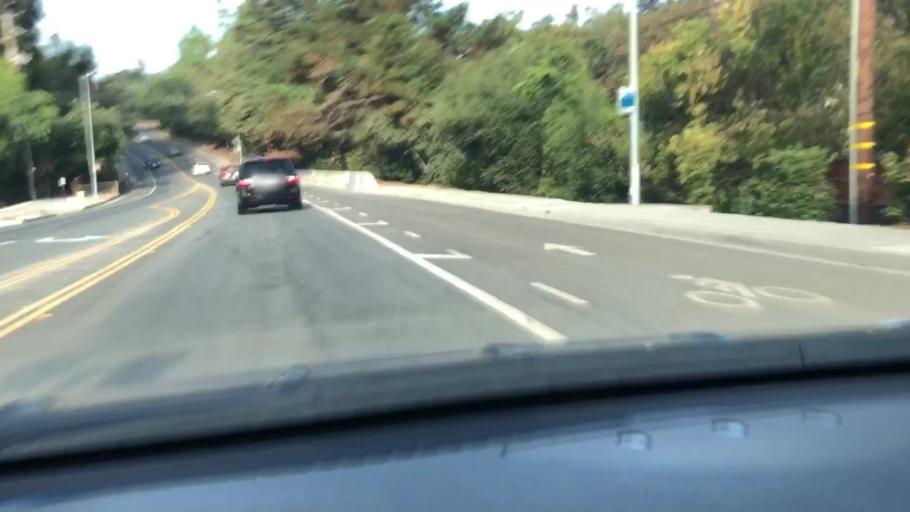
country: US
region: California
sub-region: Santa Clara County
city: Cupertino
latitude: 37.3230
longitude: -122.0605
